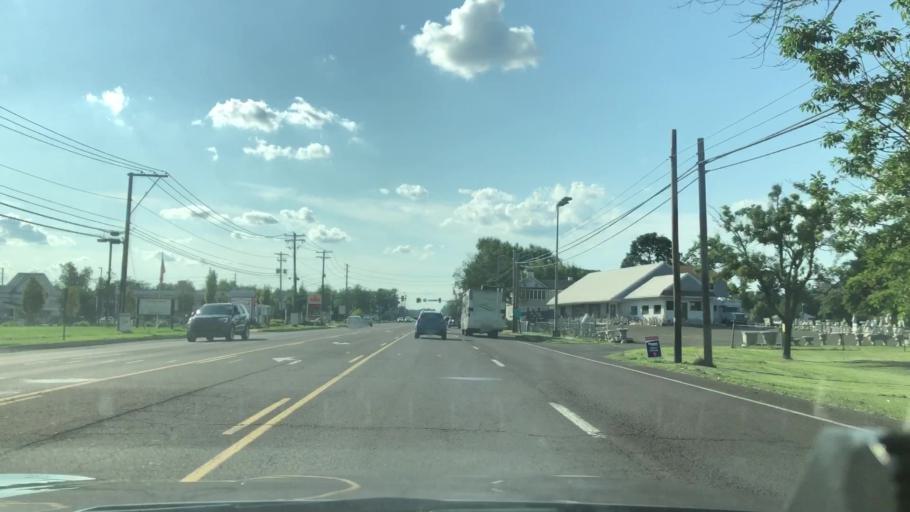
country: US
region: Pennsylvania
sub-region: Montgomery County
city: Hatfield
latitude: 40.2974
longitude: -75.2823
